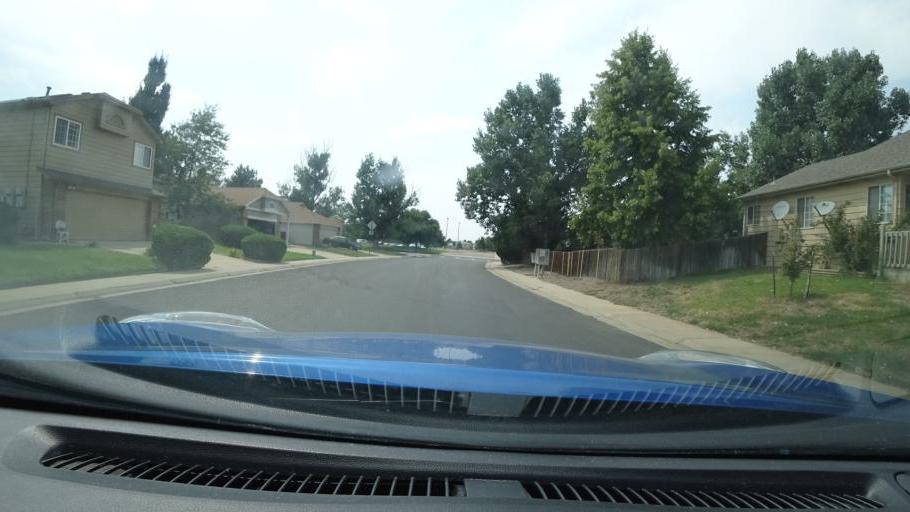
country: US
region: Colorado
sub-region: Adams County
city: Aurora
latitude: 39.7793
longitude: -104.7485
